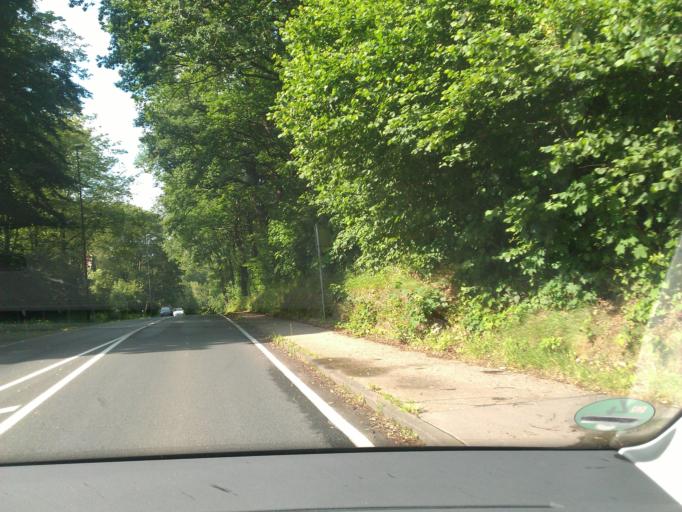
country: DE
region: North Rhine-Westphalia
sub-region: Regierungsbezirk Koln
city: Aachen
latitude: 50.7251
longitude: 6.0897
